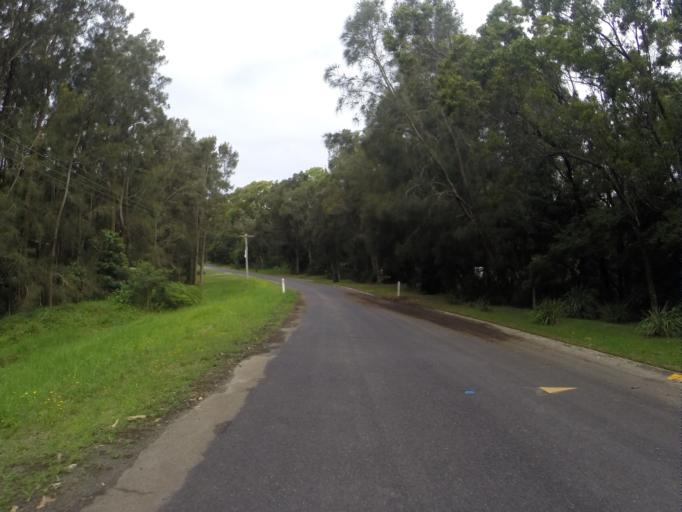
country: AU
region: New South Wales
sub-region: Eurobodalla
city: Broulee
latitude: -35.8297
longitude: 150.2230
